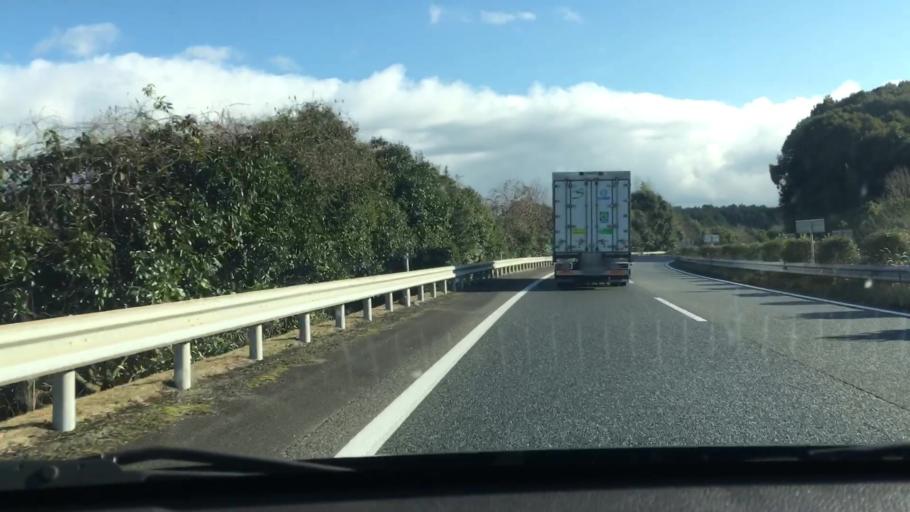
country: JP
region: Kumamoto
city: Hitoyoshi
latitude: 32.1698
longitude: 130.7922
